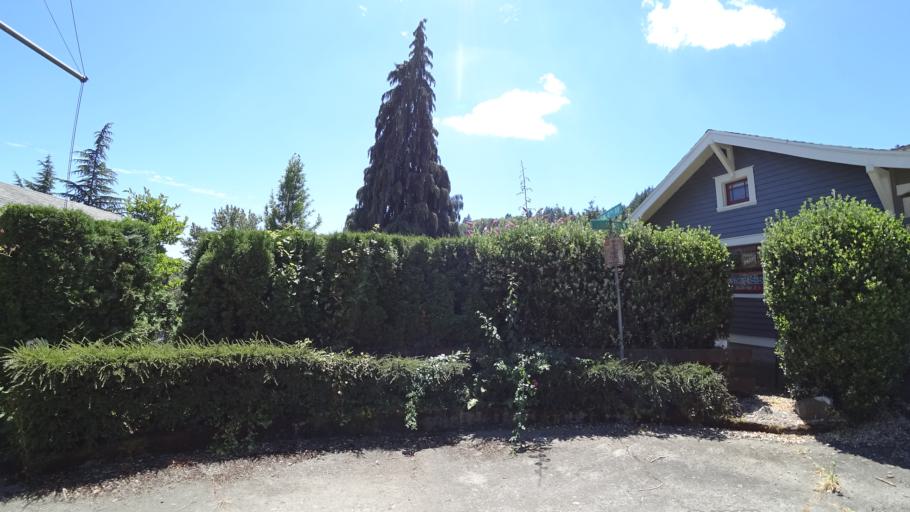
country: US
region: Oregon
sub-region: Multnomah County
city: Portland
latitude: 45.4905
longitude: -122.6825
